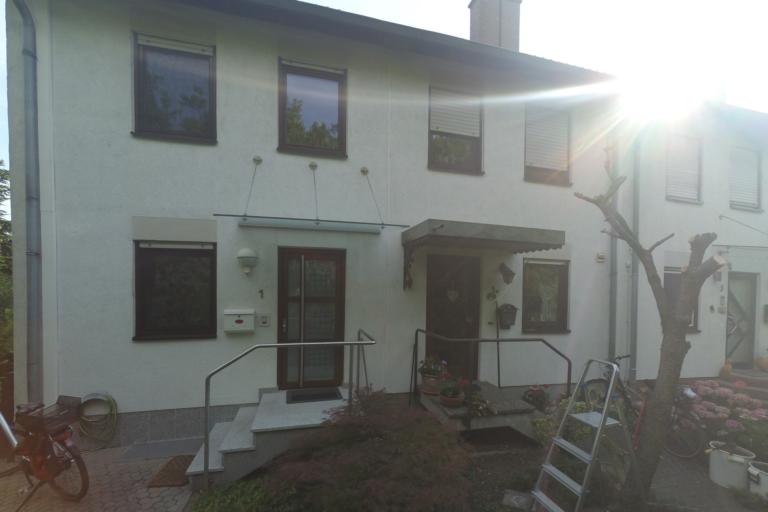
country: DE
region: Rheinland-Pfalz
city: Gartenstadt
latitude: 49.4516
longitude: 8.4052
